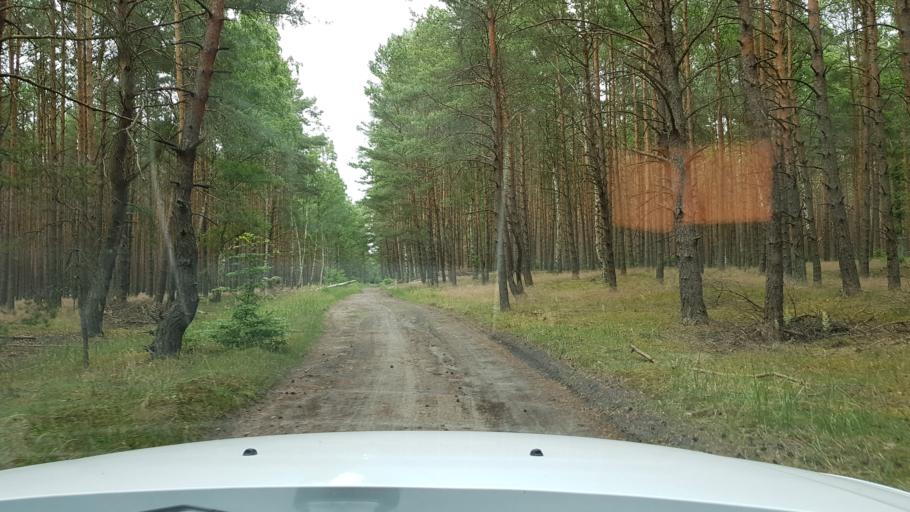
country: PL
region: West Pomeranian Voivodeship
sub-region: Powiat mysliborski
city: Boleszkowice
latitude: 52.6477
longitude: 14.5572
